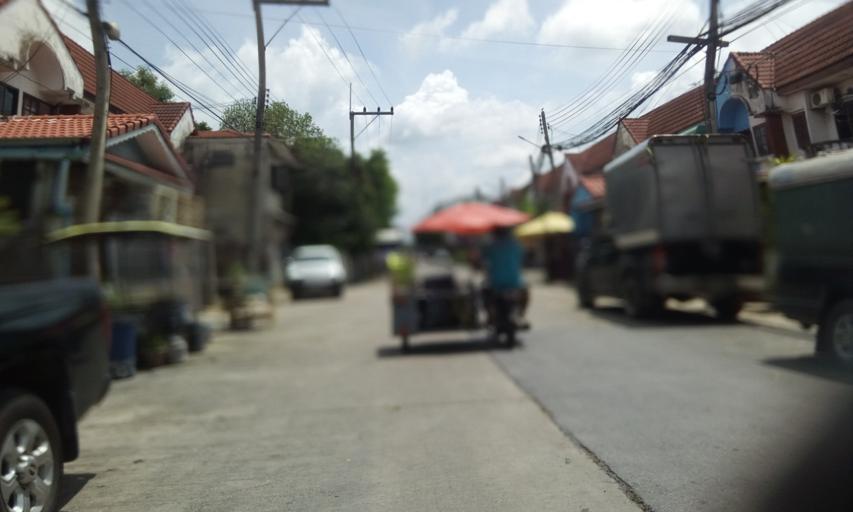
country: TH
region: Pathum Thani
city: Nong Suea
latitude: 14.0588
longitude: 100.8508
